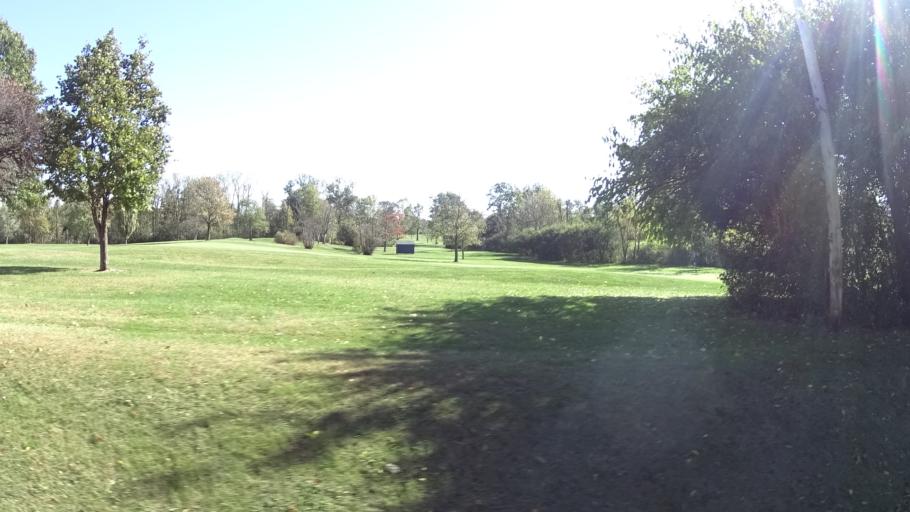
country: US
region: Ohio
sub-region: Lorain County
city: Oberlin
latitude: 41.2826
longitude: -82.2387
